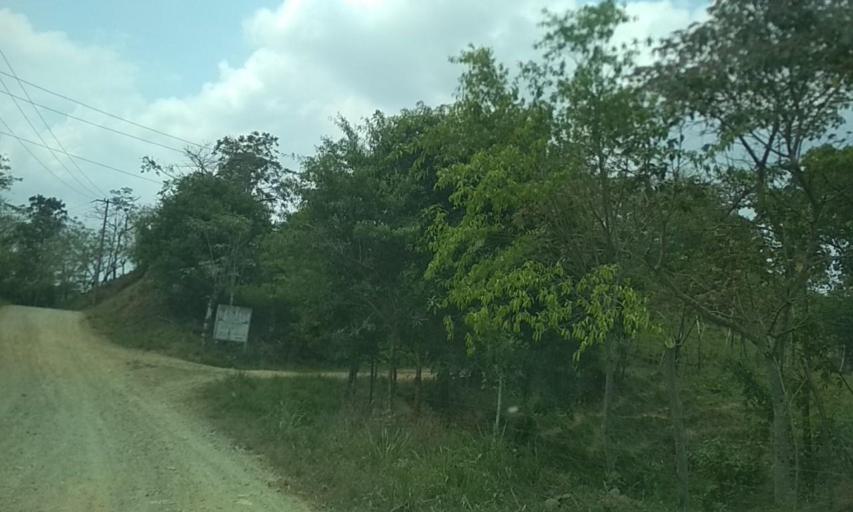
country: MX
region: Tabasco
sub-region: Huimanguillo
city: Francisco Rueda
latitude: 17.6033
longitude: -93.8046
